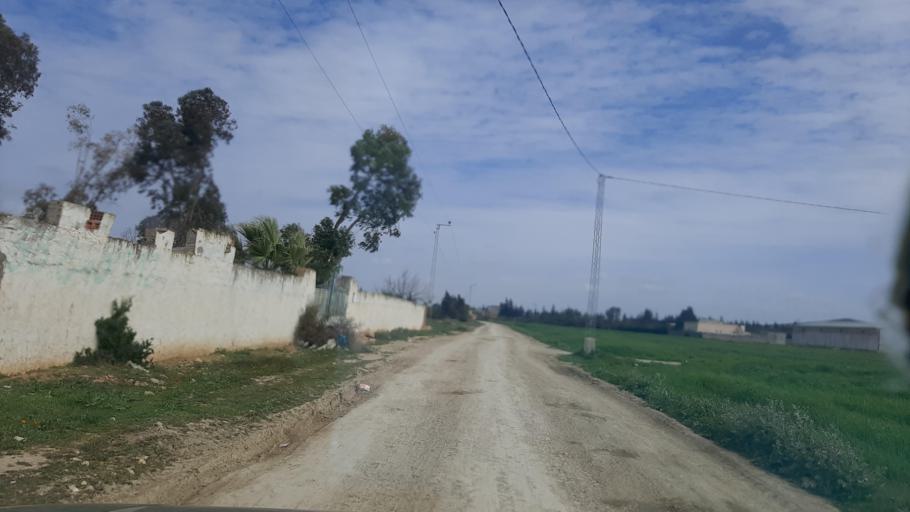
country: TN
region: Tunis
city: Oued Lill
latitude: 36.6959
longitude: 10.0004
